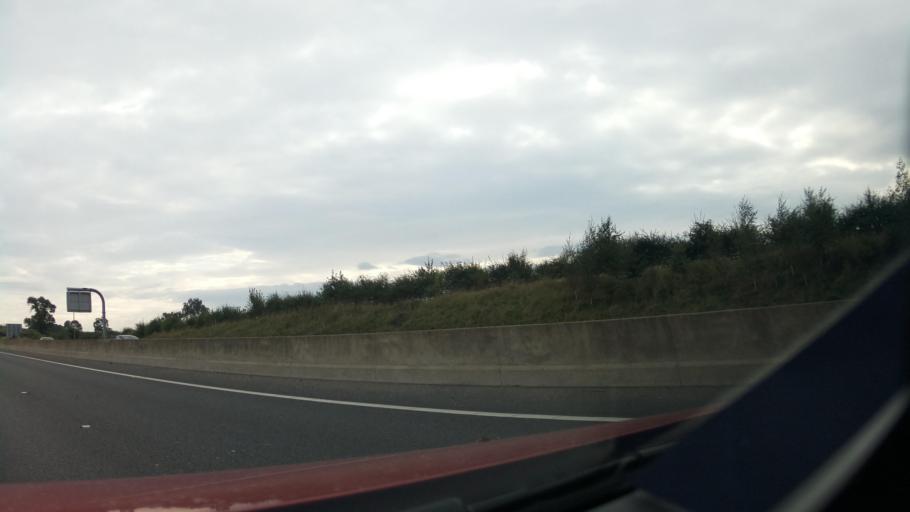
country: GB
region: England
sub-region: Darlington
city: High Coniscliffe
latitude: 54.4564
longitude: -1.6677
